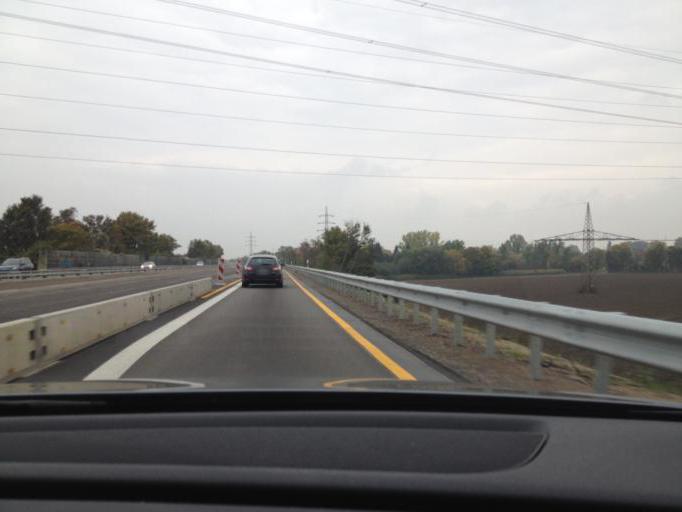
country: DE
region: Rheinland-Pfalz
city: Frankenthal
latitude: 49.5517
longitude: 8.3859
